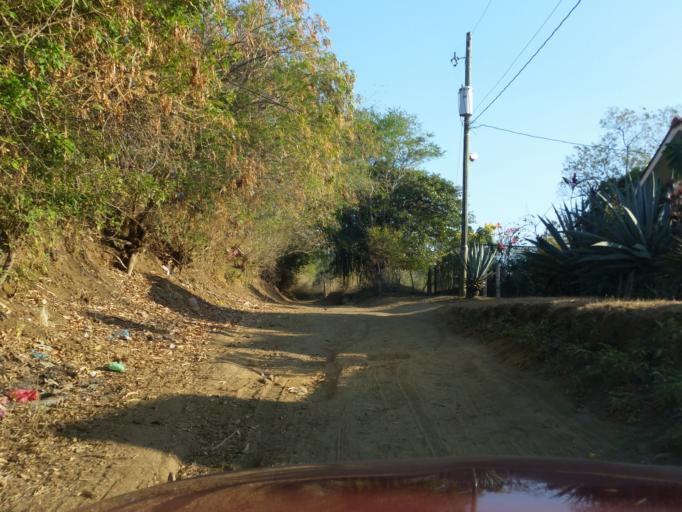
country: NI
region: Managua
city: Managua
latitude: 12.0785
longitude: -86.2585
